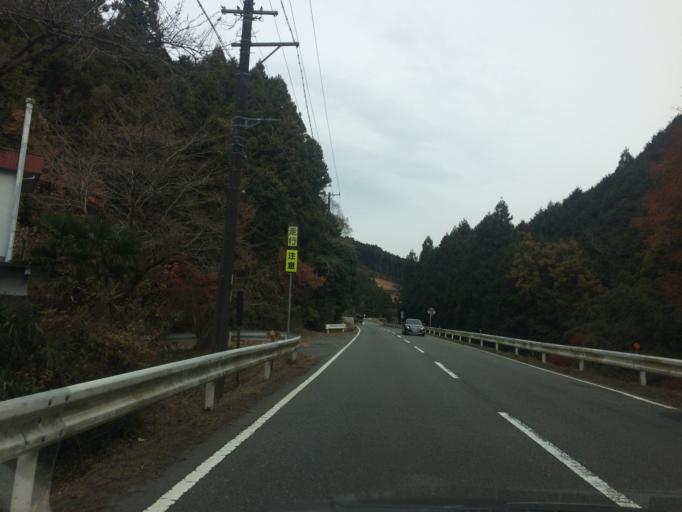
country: JP
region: Shizuoka
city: Fujinomiya
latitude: 35.1693
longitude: 138.5226
